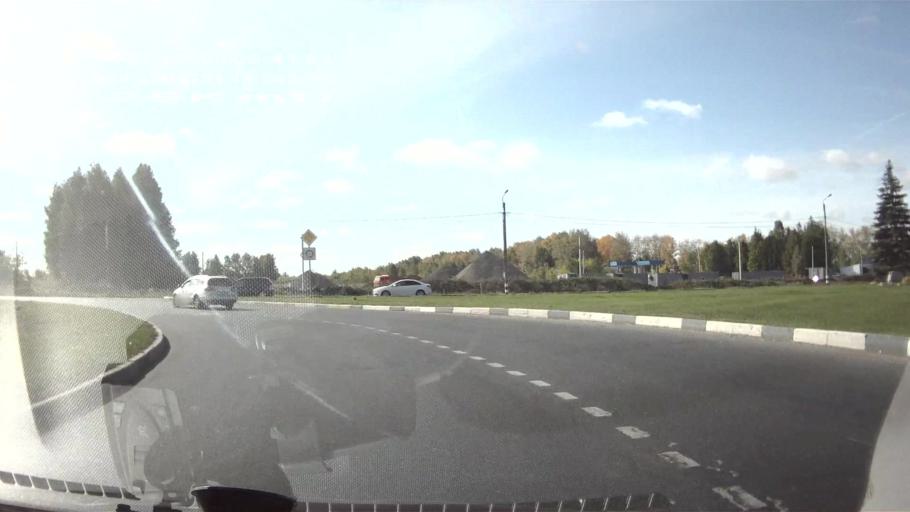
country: RU
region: Ulyanovsk
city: Isheyevka
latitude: 54.2909
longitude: 48.2540
